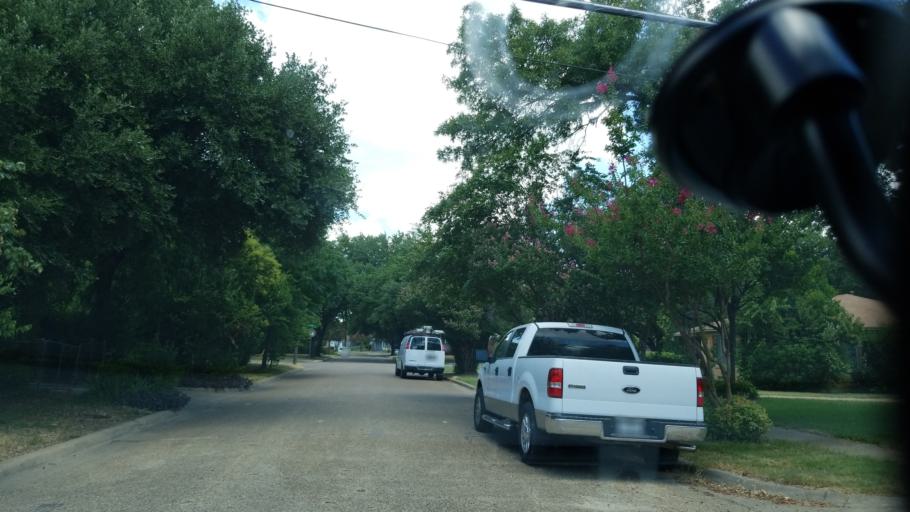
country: US
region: Texas
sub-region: Dallas County
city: Cockrell Hill
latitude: 32.7124
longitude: -96.8452
